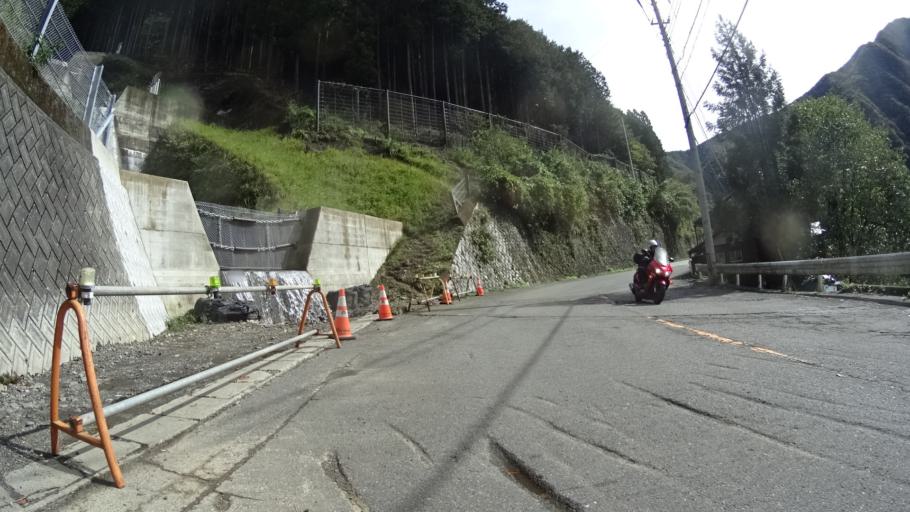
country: JP
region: Yamanashi
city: Otsuki
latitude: 35.7886
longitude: 138.9442
